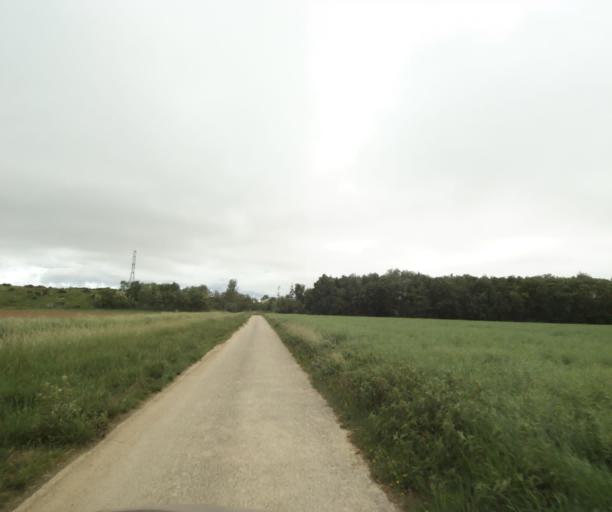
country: FR
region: Rhone-Alpes
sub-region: Departement de l'Ain
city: Tramoyes
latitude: 45.8608
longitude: 4.9536
